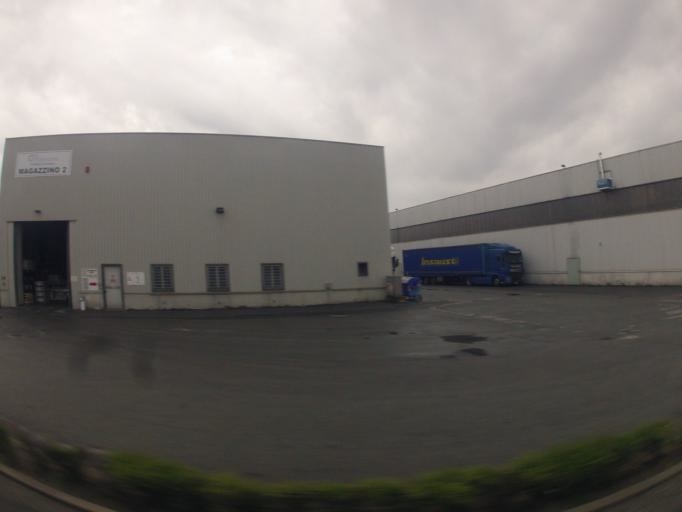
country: IT
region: Piedmont
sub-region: Provincia di Cuneo
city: Casalgrasso
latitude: 44.8316
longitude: 7.6255
